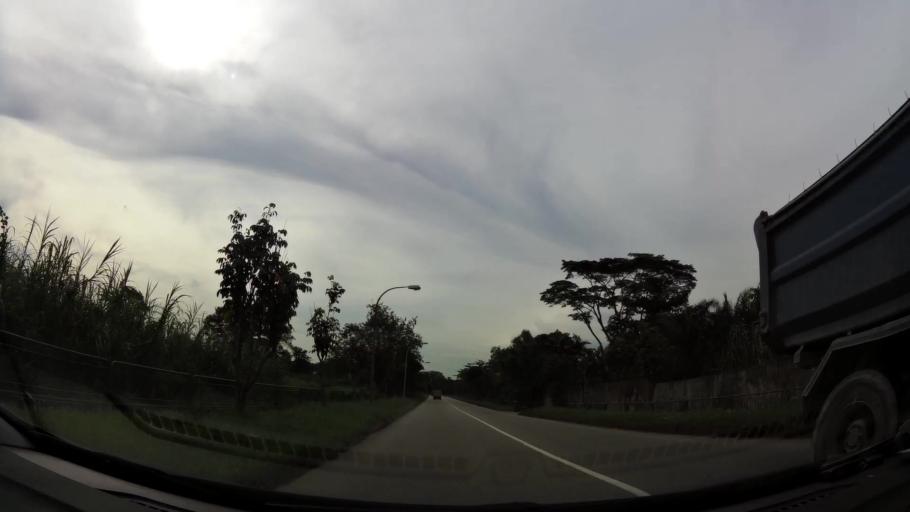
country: MY
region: Johor
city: Johor Bahru
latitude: 1.4300
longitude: 103.7191
